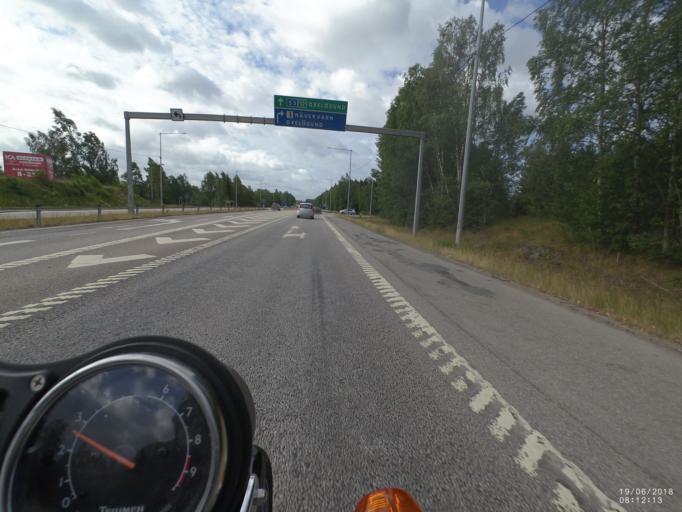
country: SE
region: Soedermanland
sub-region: Nykopings Kommun
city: Nykoping
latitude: 58.7288
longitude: 17.0059
